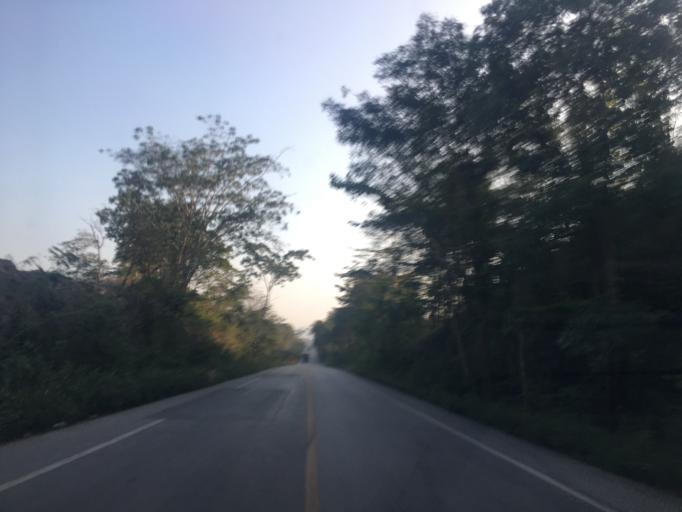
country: TH
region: Lampang
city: Ngao
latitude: 18.6561
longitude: 100.0177
